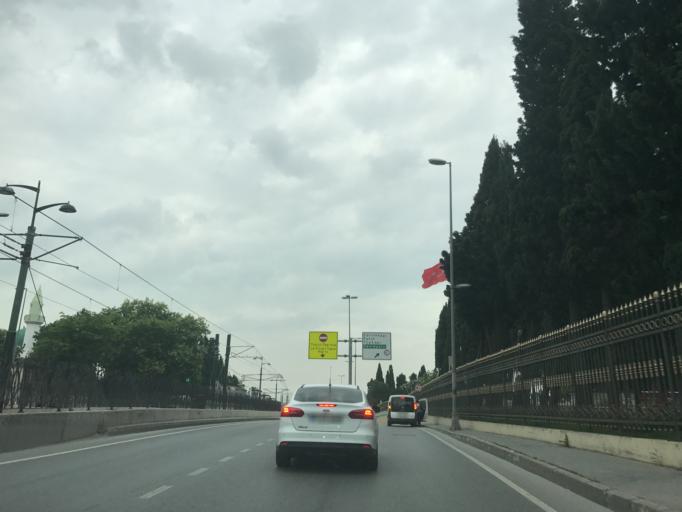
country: TR
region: Istanbul
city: Istanbul
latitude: 41.0346
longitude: 28.9268
